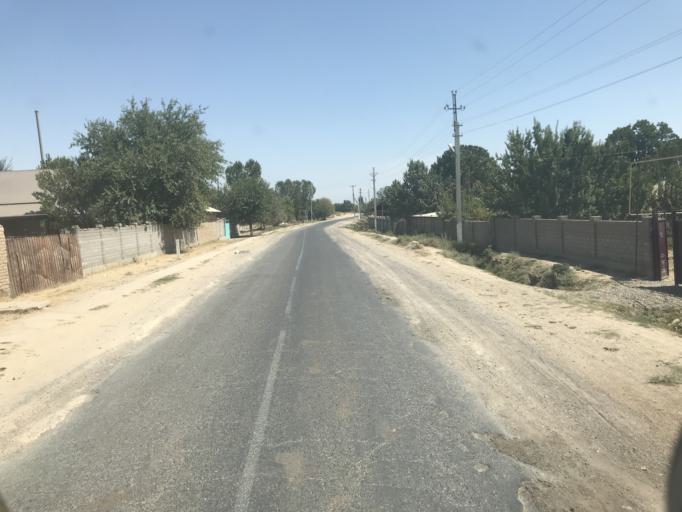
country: UZ
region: Toshkent
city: Yangiyul
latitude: 41.3766
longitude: 68.8033
